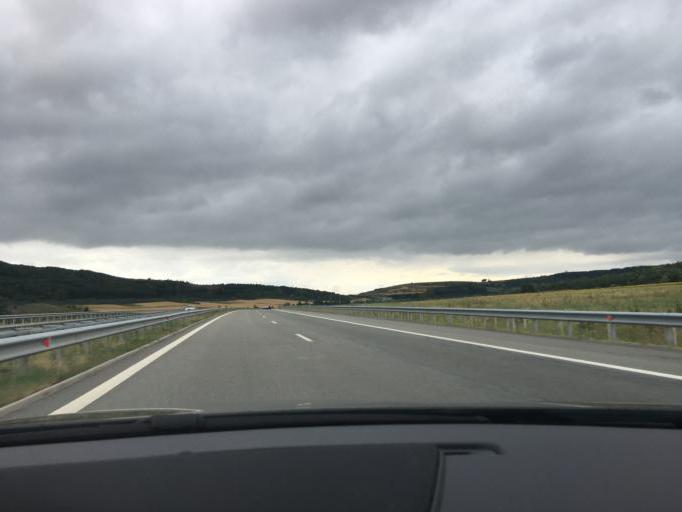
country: BG
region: Kyustendil
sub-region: Obshtina Bobovdol
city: Bobovdol
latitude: 42.3992
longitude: 23.1206
